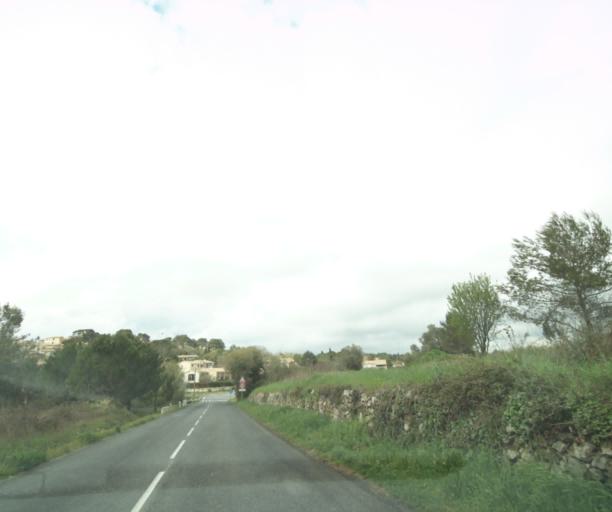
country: FR
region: Languedoc-Roussillon
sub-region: Departement de l'Herault
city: Murviel-les-Montpellier
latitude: 43.6012
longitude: 3.7394
